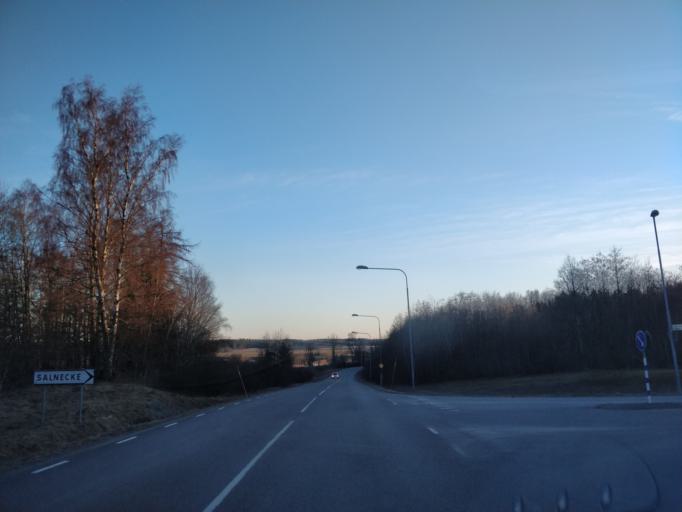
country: SE
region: Uppsala
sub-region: Enkopings Kommun
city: Orsundsbro
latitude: 59.7414
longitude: 17.3327
